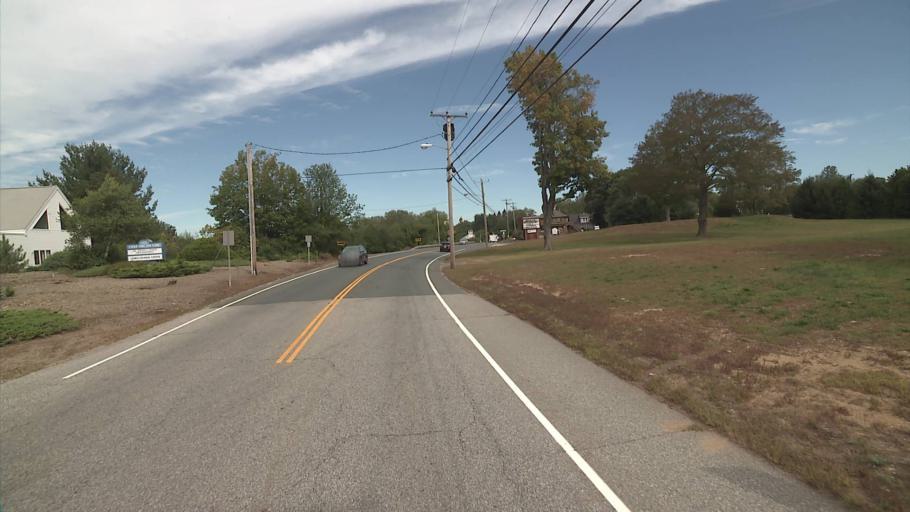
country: US
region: Connecticut
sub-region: Tolland County
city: Mansfield City
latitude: 41.7395
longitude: -72.2596
